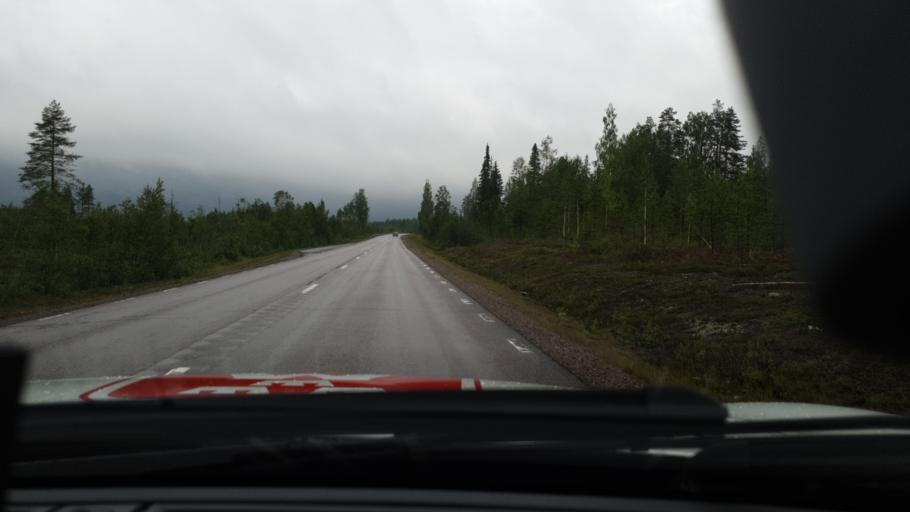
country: SE
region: Norrbotten
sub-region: Kalix Kommun
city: Toere
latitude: 65.9914
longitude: 22.6935
